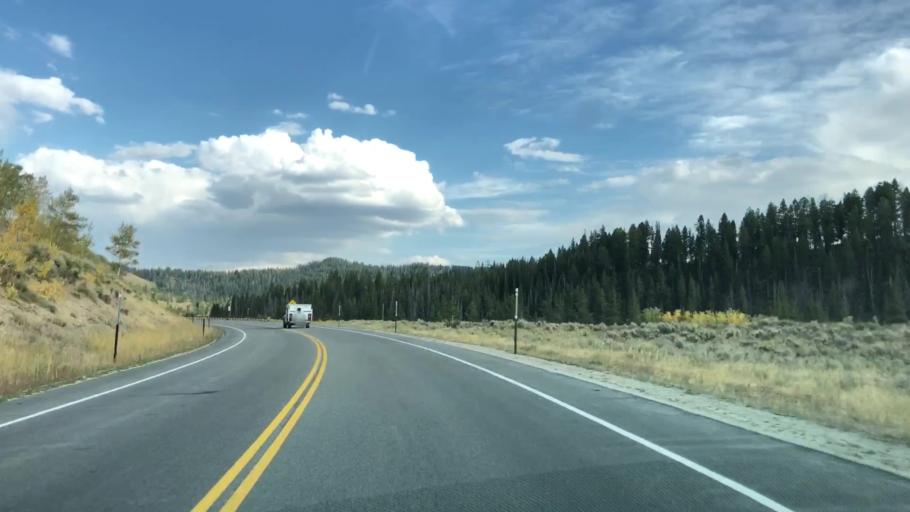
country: US
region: Wyoming
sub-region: Sublette County
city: Pinedale
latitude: 43.1361
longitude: -110.2320
